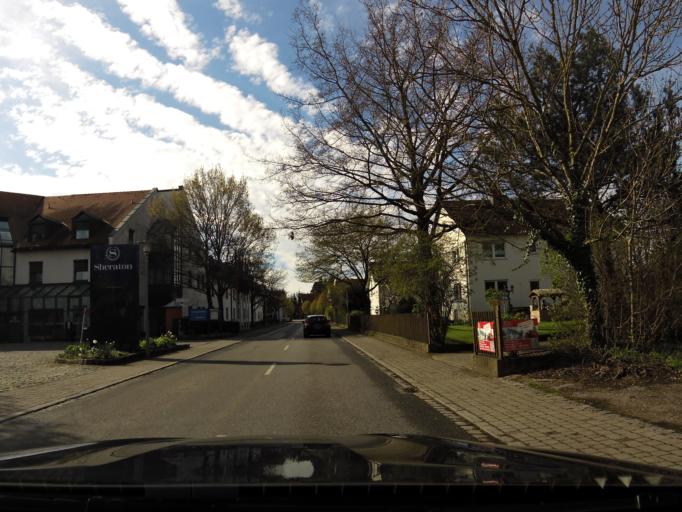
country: DE
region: Bavaria
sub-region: Upper Bavaria
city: Oberding
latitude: 48.3428
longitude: 11.8326
